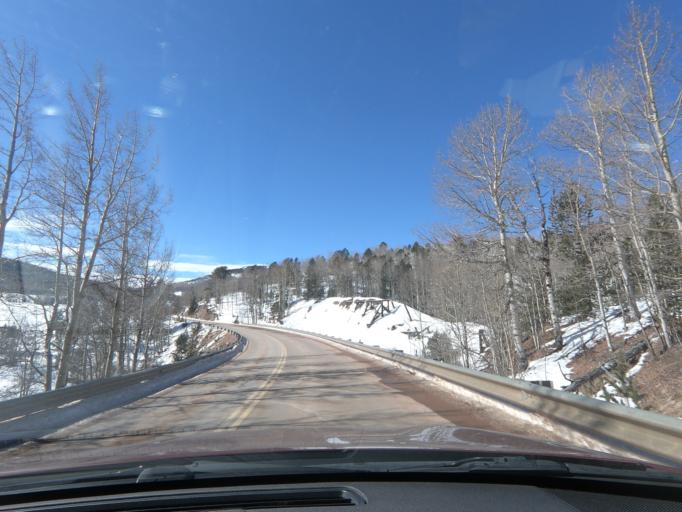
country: US
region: Colorado
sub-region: Teller County
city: Cripple Creek
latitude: 38.7433
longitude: -105.1064
